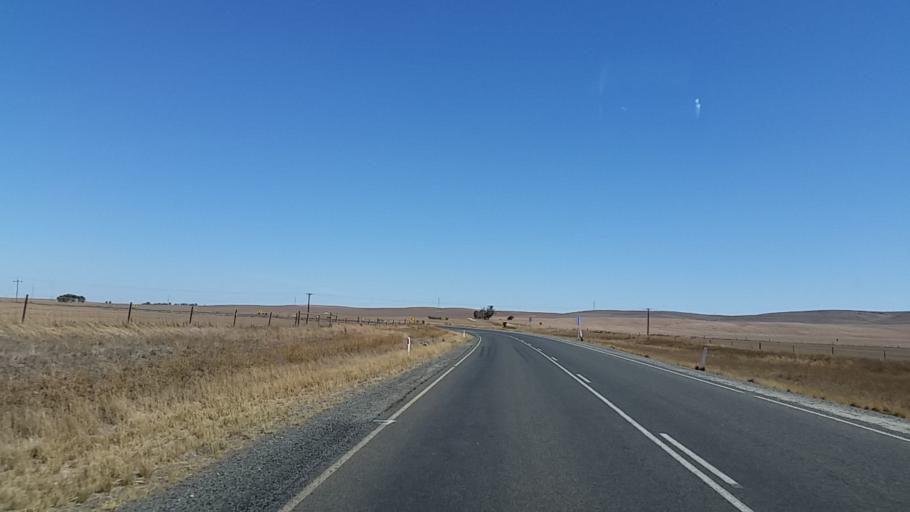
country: AU
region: South Australia
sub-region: Clare and Gilbert Valleys
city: Clare
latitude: -33.6825
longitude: 138.9080
